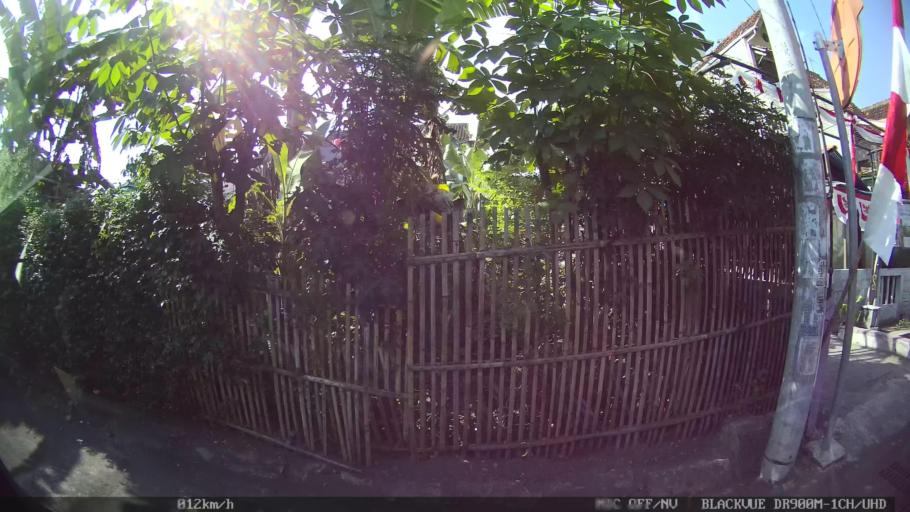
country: ID
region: Daerah Istimewa Yogyakarta
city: Sewon
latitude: -7.8308
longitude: 110.3913
